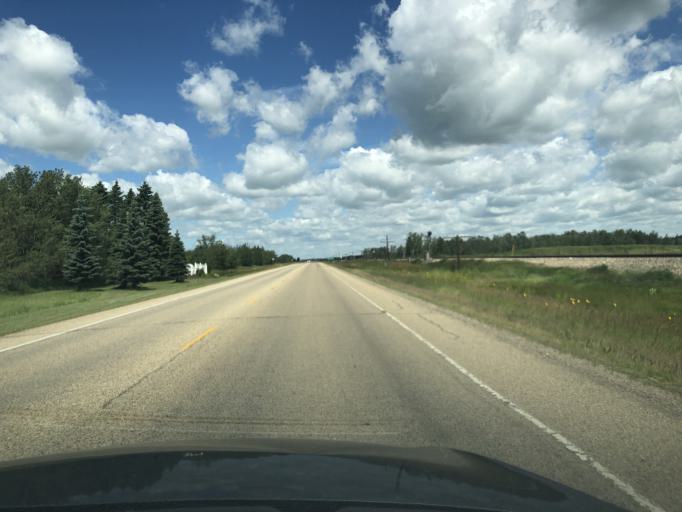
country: CA
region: Alberta
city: Millet
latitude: 53.0993
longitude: -113.4733
